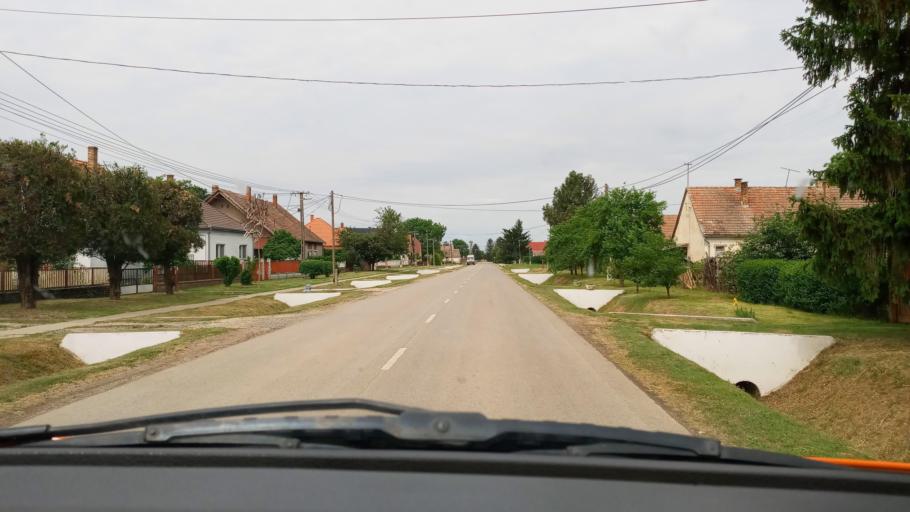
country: HU
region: Baranya
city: Vajszlo
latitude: 45.9076
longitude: 18.0368
